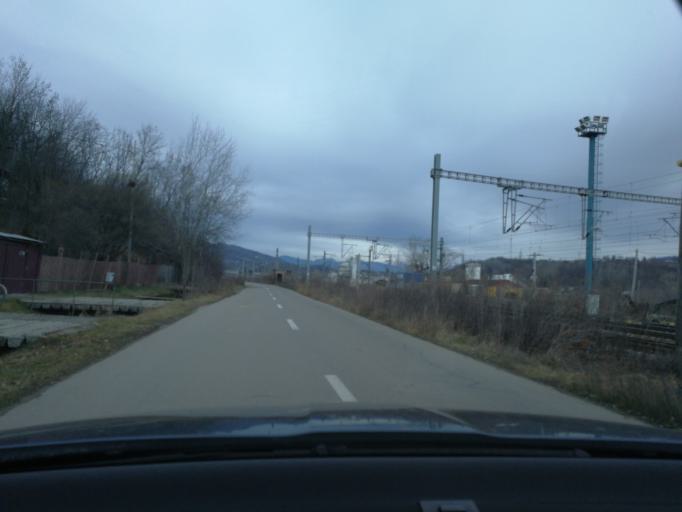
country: RO
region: Prahova
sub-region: Comuna Cornu
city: Cornu de Jos
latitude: 45.1361
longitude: 25.7046
